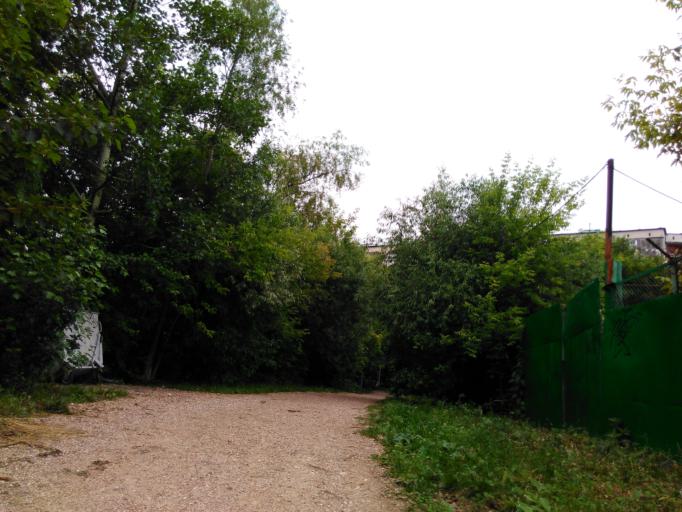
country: RU
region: Moscow
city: Yasenevo
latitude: 55.6311
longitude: 37.5346
